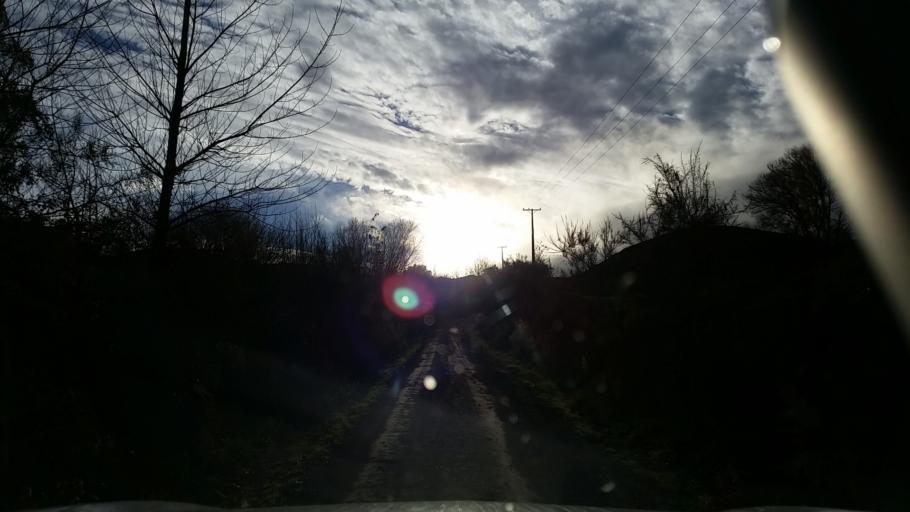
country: NZ
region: Bay of Plenty
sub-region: Rotorua District
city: Rotorua
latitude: -38.2992
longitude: 176.2757
